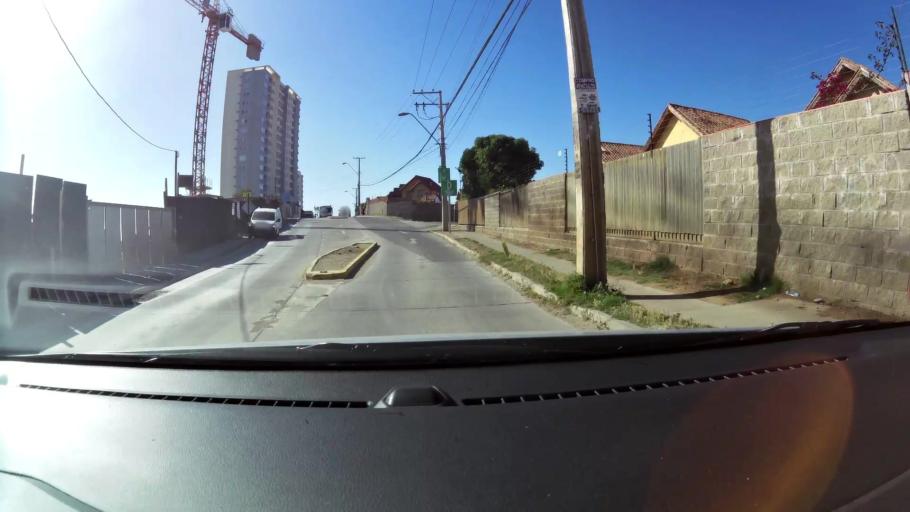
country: CL
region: Valparaiso
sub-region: Provincia de Valparaiso
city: Vina del Mar
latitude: -33.0422
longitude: -71.5559
